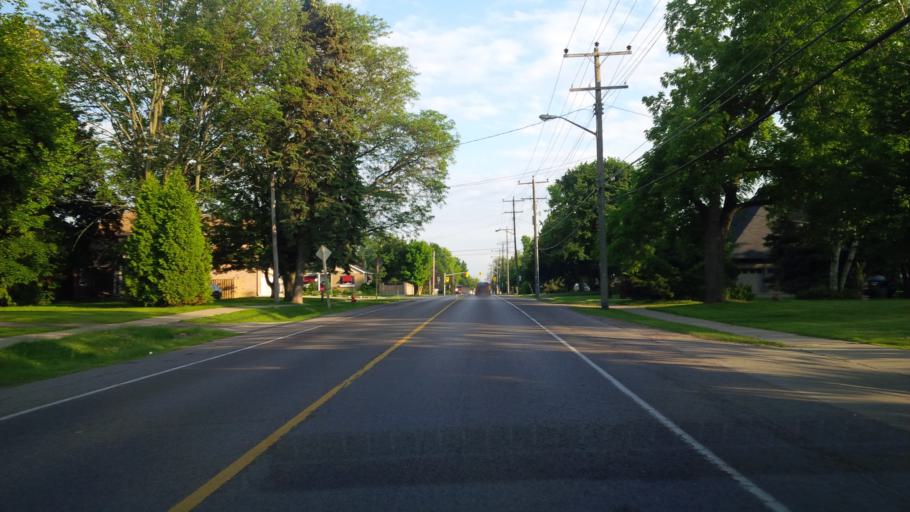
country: CA
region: Ontario
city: Ancaster
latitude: 43.2160
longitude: -79.9867
